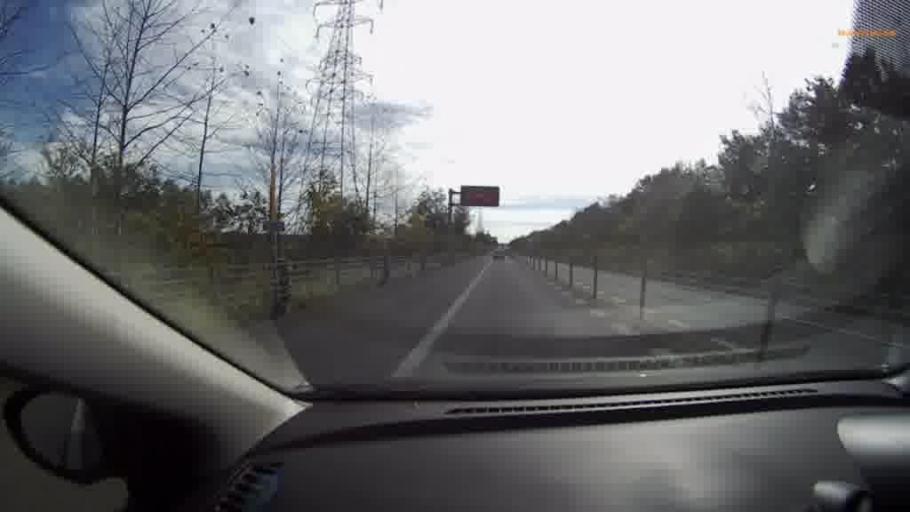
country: JP
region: Hokkaido
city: Kushiro
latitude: 43.0253
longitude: 144.4112
